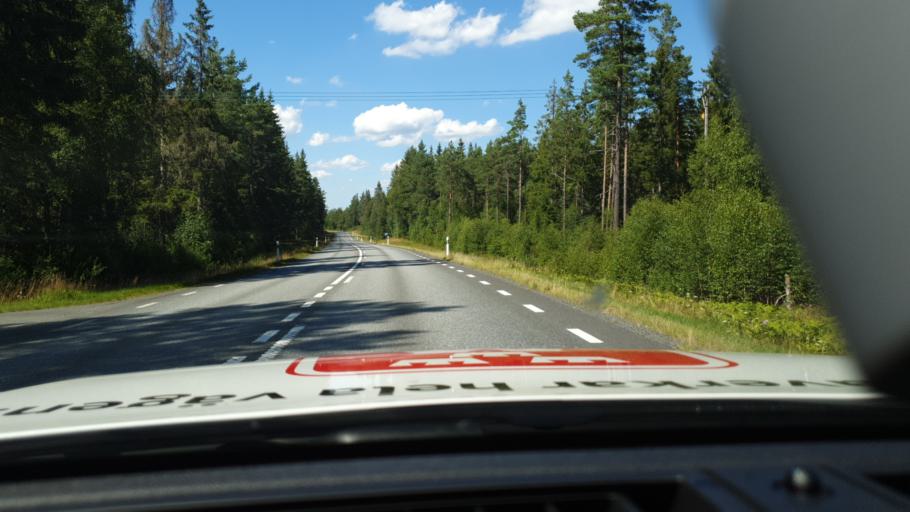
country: SE
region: Joenkoeping
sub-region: Savsjo Kommun
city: Vrigstad
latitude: 57.3940
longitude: 14.3800
